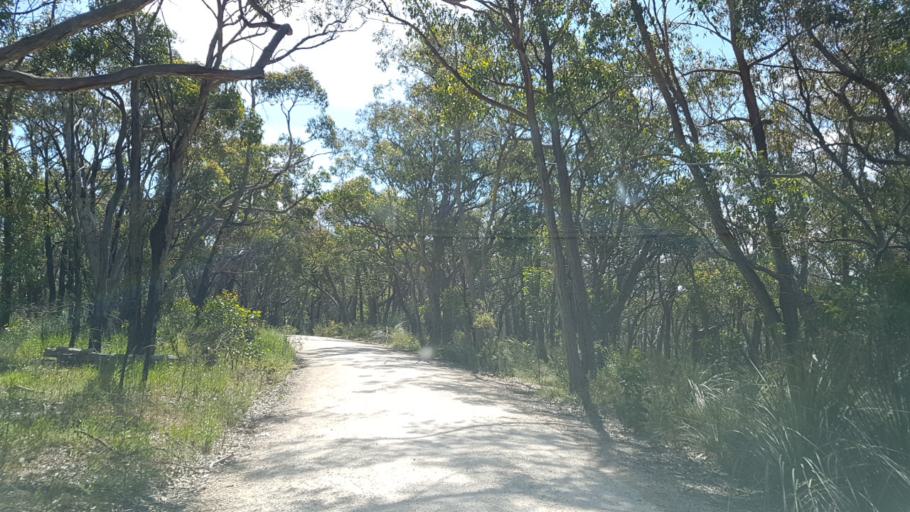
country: AU
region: South Australia
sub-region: Adelaide Hills
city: Adelaide Hills
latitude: -34.9042
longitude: 138.7324
